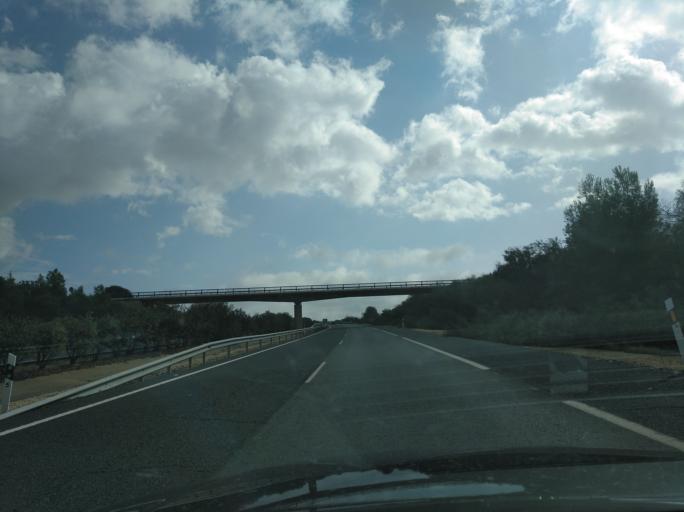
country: ES
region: Andalusia
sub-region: Provincia de Huelva
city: Cartaya
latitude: 37.3271
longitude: -7.1361
